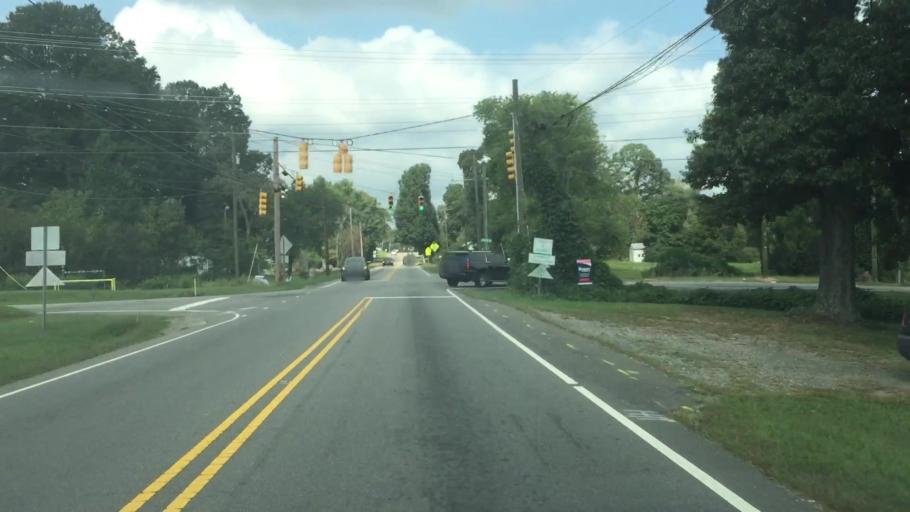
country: US
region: North Carolina
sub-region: Gaston County
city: Davidson
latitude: 35.5428
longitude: -80.8473
